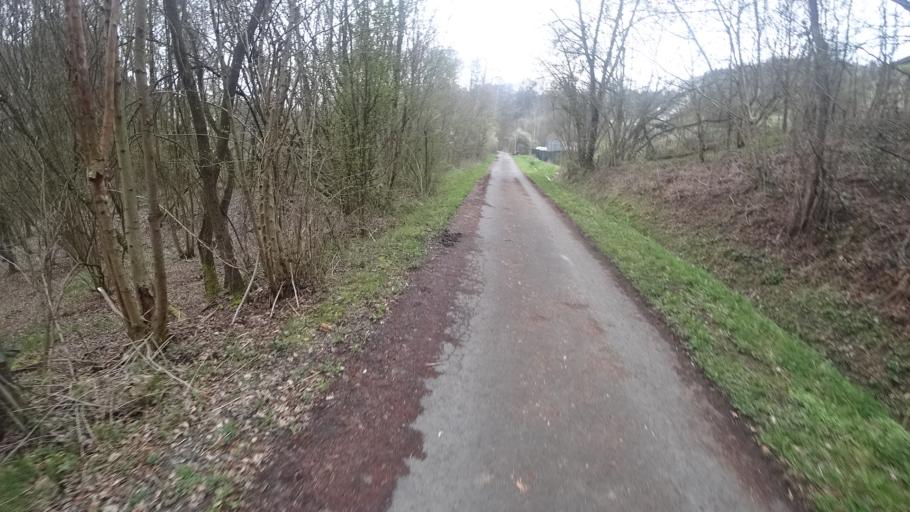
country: DE
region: Rheinland-Pfalz
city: Elben
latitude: 50.7539
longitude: 7.8320
